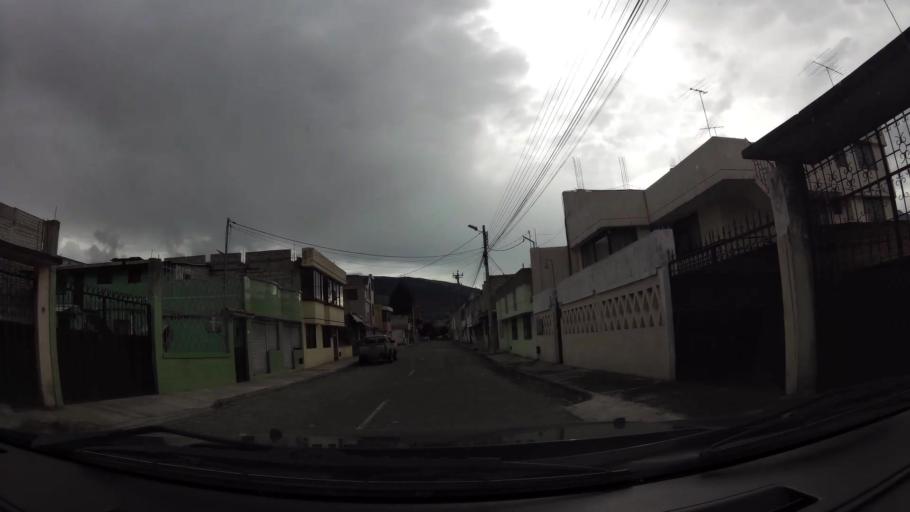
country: EC
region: Pichincha
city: Quito
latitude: -0.3035
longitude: -78.5516
